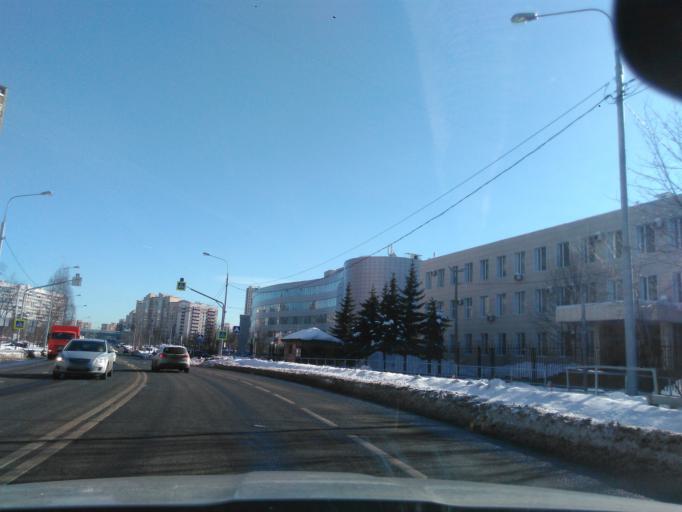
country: RU
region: Moscow
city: Zelenograd
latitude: 55.9848
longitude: 37.1723
